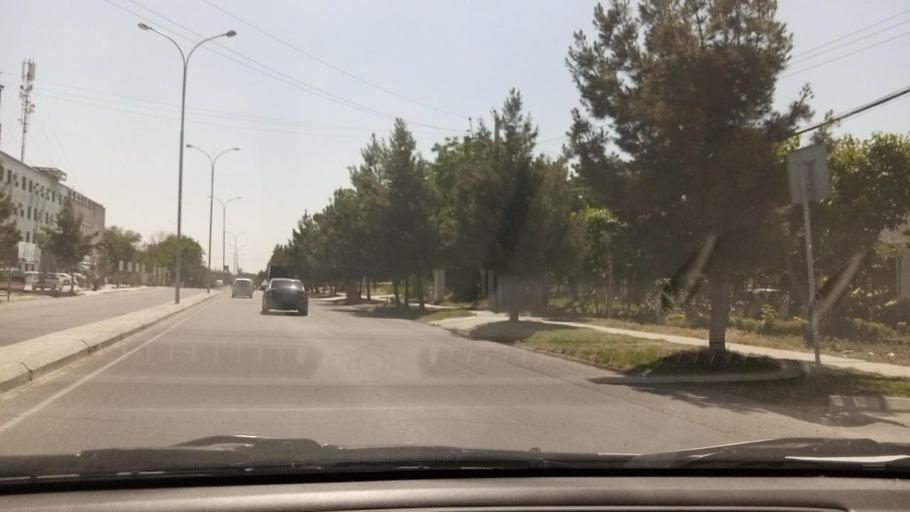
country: UZ
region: Toshkent
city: Urtaowul
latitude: 41.2251
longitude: 69.1786
